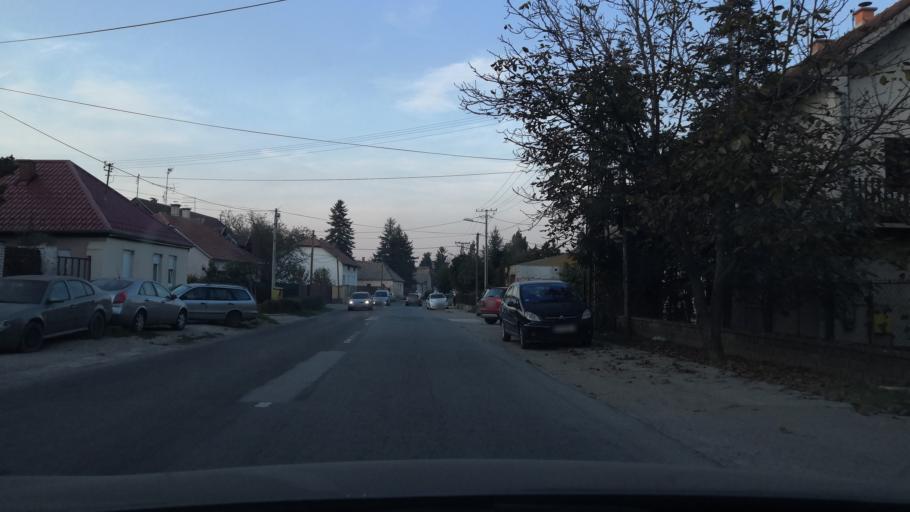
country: RS
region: Autonomna Pokrajina Vojvodina
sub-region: Juznobacki Okrug
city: Petrovaradin
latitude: 45.2340
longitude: 19.8848
